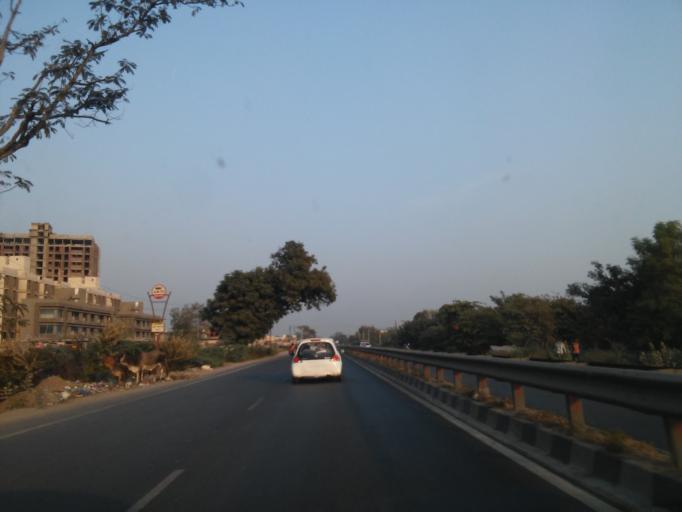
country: IN
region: Gujarat
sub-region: Ahmadabad
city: Sarkhej
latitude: 22.9880
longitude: 72.4612
